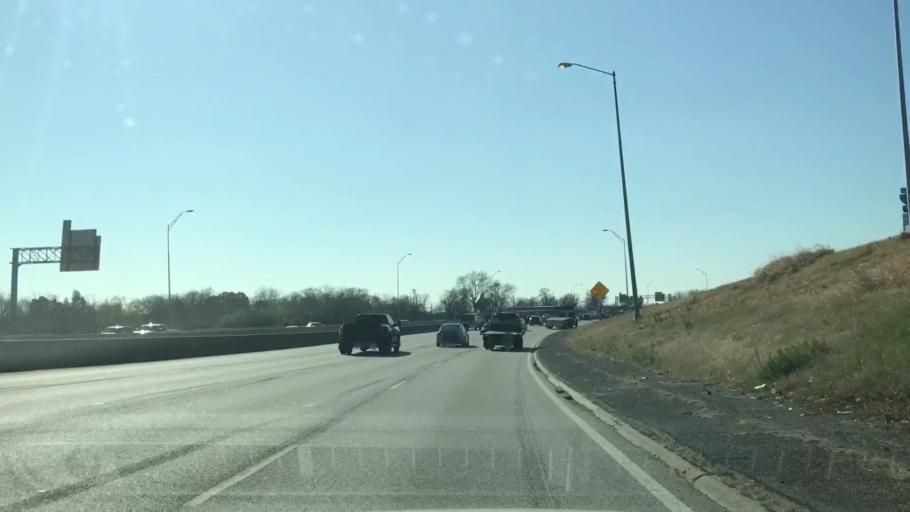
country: US
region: Texas
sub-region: Dallas County
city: Dallas
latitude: 32.7499
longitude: -96.8096
